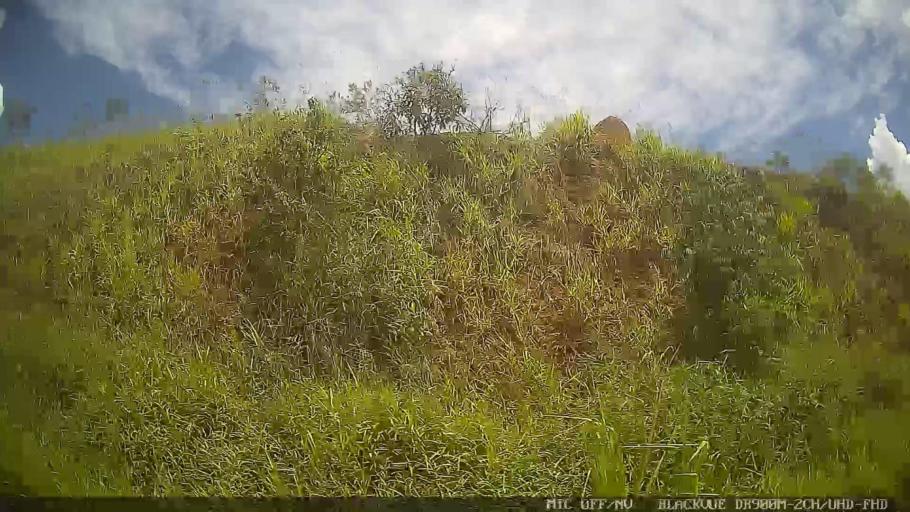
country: BR
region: Minas Gerais
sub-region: Extrema
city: Extrema
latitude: -22.7255
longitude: -46.4120
